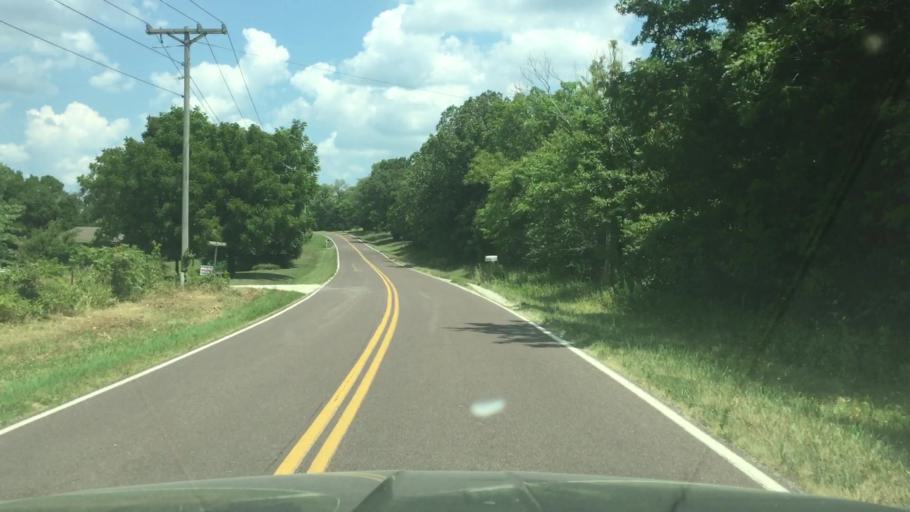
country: US
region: Missouri
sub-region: Miller County
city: Tuscumbia
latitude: 38.1047
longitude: -92.4736
